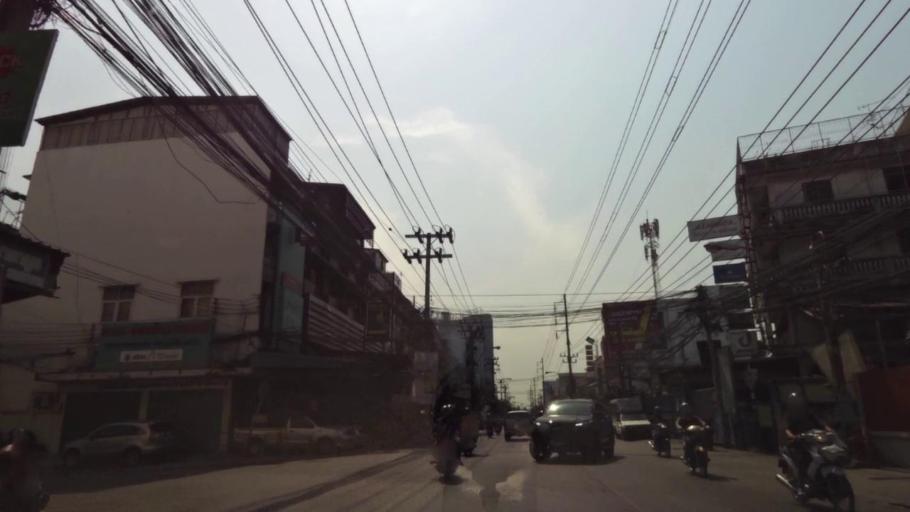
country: TH
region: Bangkok
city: Phra Khanong
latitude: 13.6527
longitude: 100.5932
